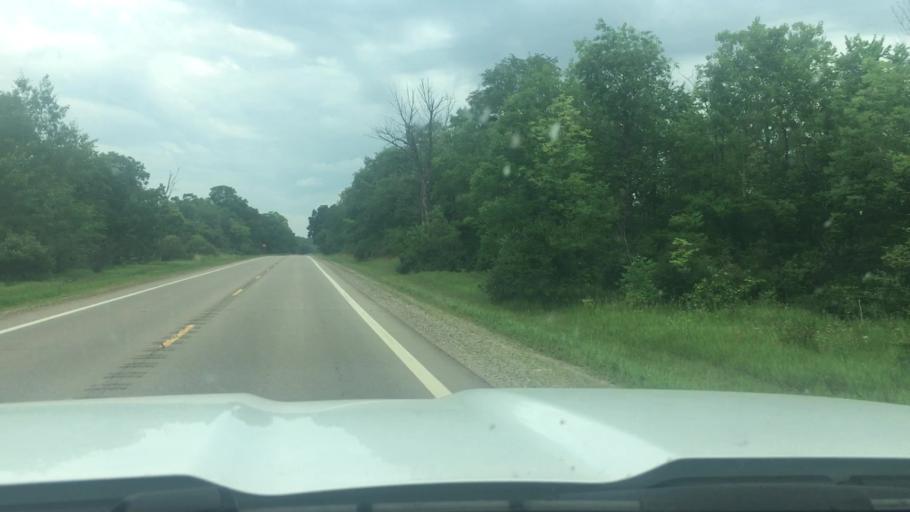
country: US
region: Michigan
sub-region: Ionia County
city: Portland
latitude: 43.0011
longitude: -84.8988
